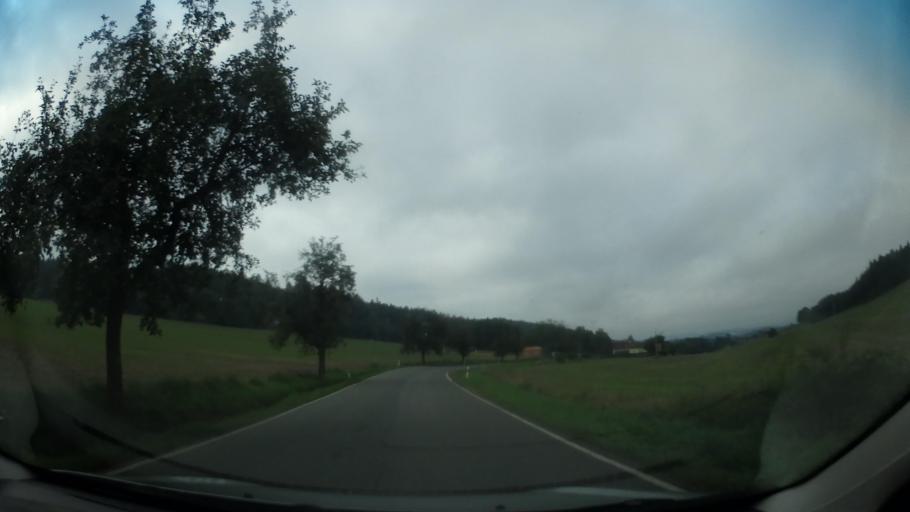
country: CZ
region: Central Bohemia
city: Neveklov
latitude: 49.7253
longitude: 14.4875
